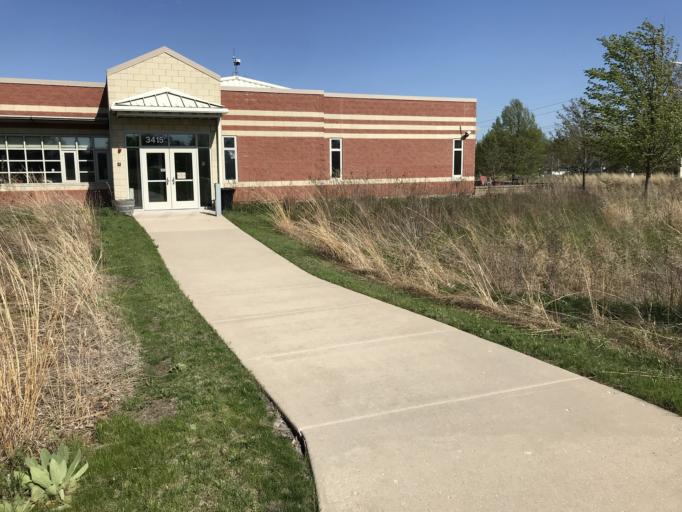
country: US
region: Illinois
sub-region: Will County
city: Plainfield
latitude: 41.7042
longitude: -88.1880
